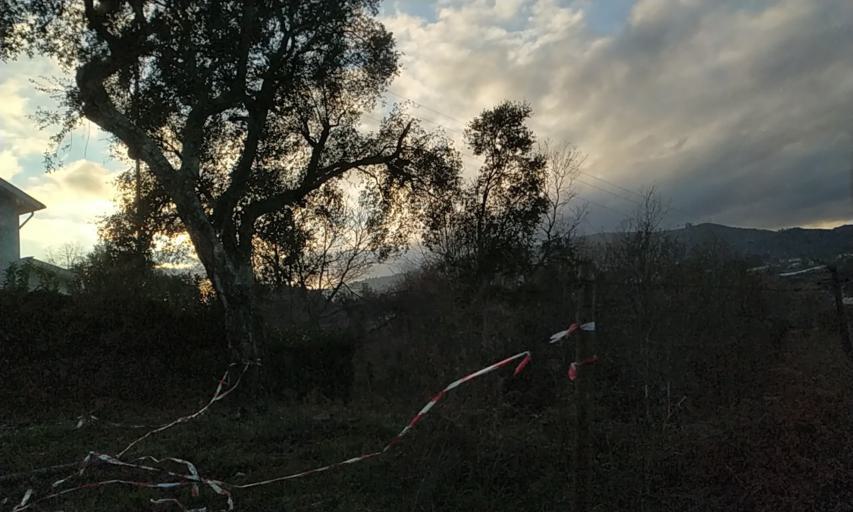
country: PT
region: Vila Real
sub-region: Mondim de Basto
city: Mondim de Basto
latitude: 41.4261
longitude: -7.9858
